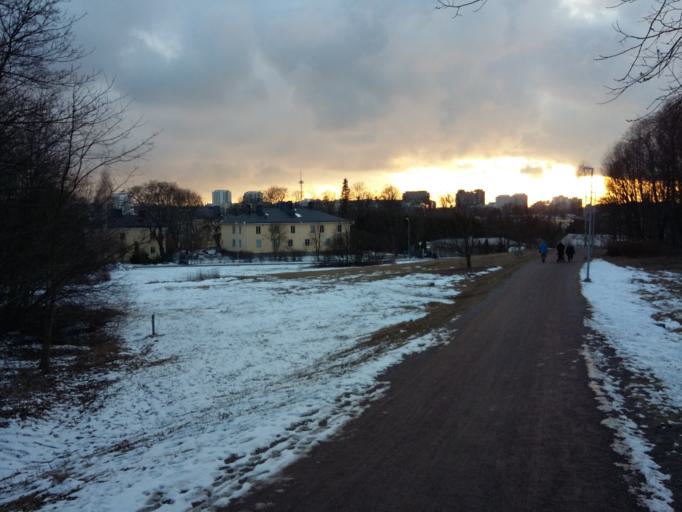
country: FI
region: Uusimaa
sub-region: Helsinki
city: Helsinki
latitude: 60.2032
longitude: 24.9603
